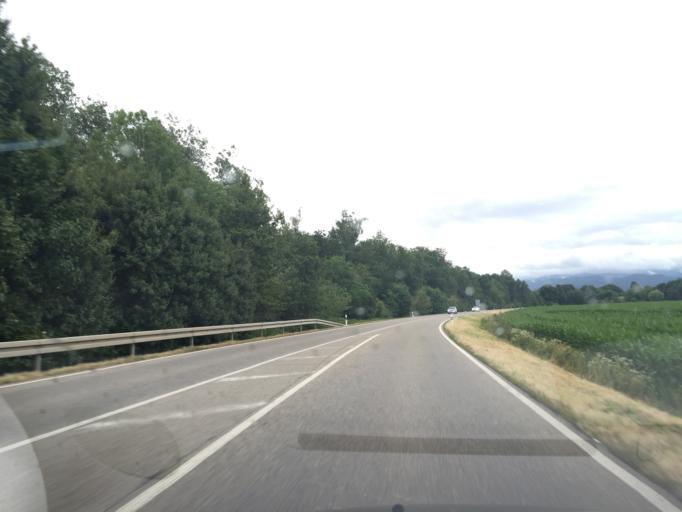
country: DE
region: Baden-Wuerttemberg
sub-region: Freiburg Region
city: Unterkrozingen
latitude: 47.9396
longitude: 7.6828
